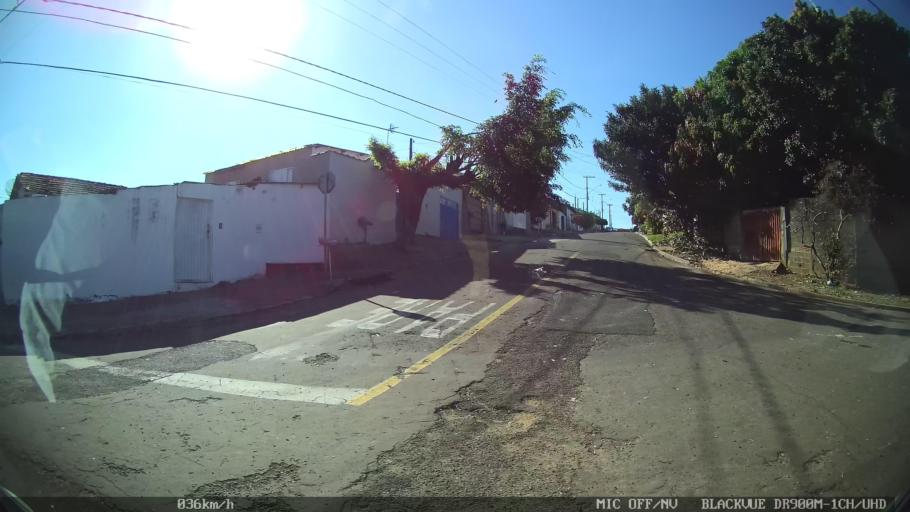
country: BR
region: Sao Paulo
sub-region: Franca
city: Franca
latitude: -20.4915
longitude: -47.4168
